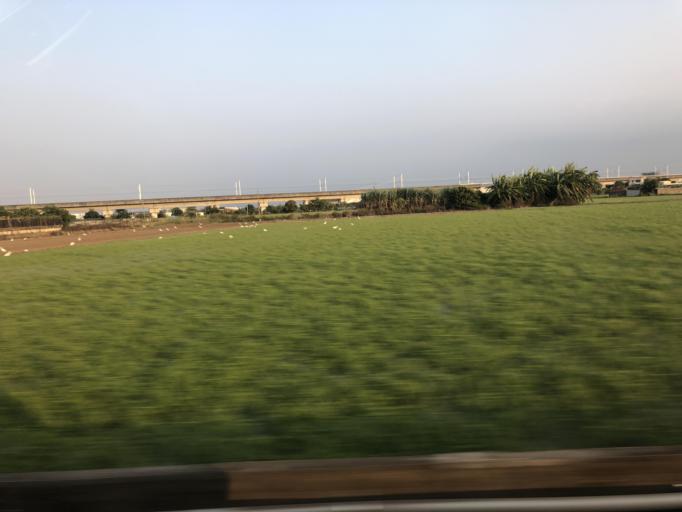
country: TW
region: Taiwan
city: Xinying
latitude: 23.1500
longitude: 120.2737
